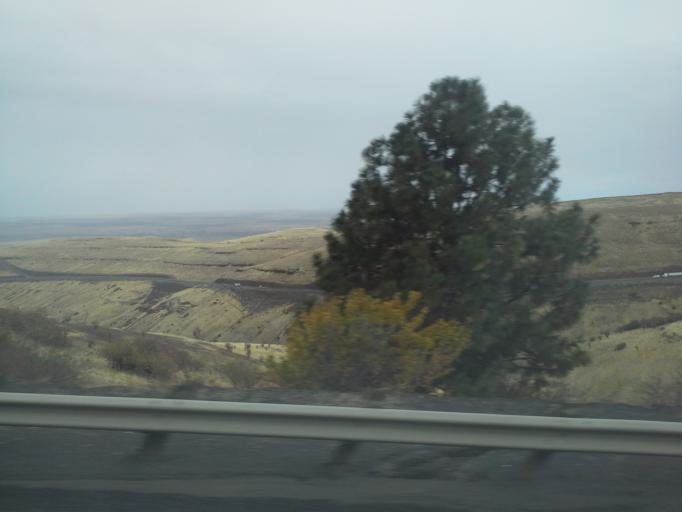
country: US
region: Oregon
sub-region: Umatilla County
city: Mission
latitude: 45.5885
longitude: -118.6181
